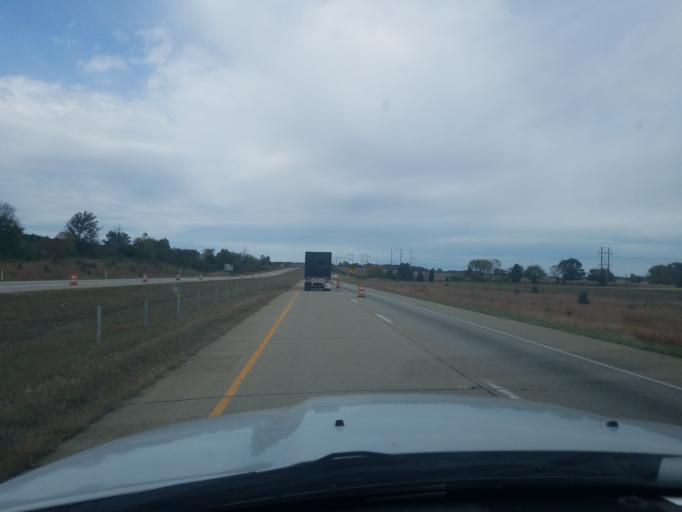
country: US
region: Indiana
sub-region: Vanderburgh County
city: Darmstadt
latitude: 38.1407
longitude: -87.4727
